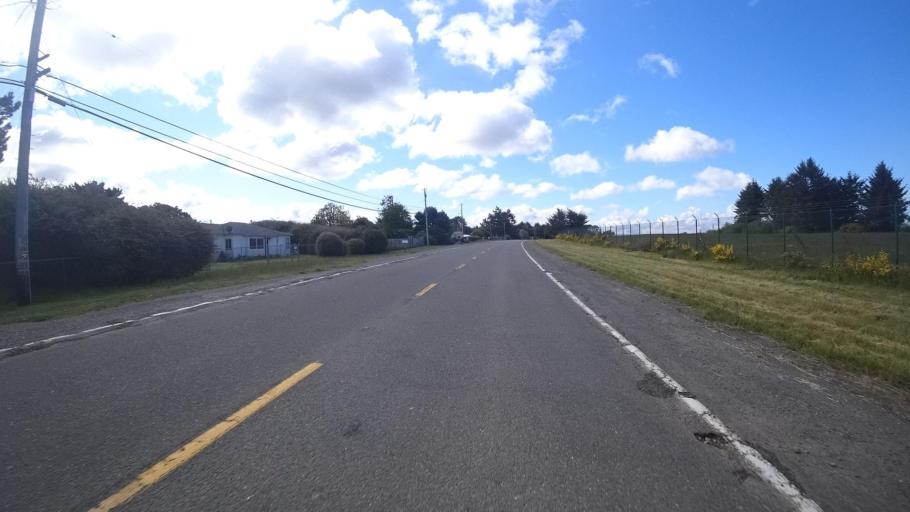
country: US
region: California
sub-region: Humboldt County
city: McKinleyville
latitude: 40.9811
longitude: -124.1017
